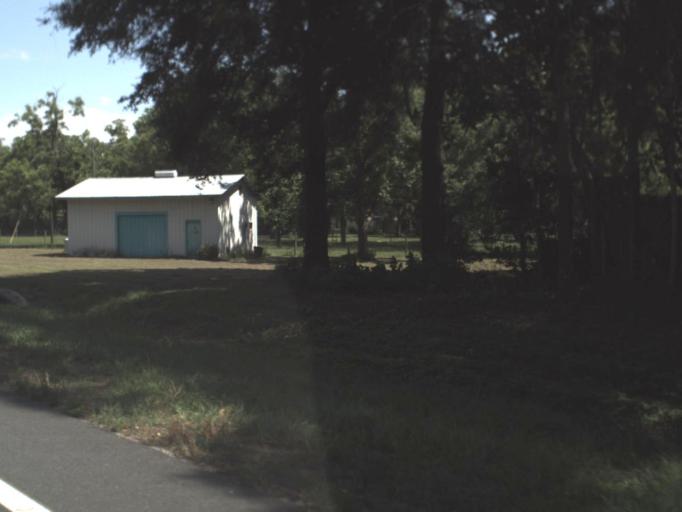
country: US
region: Florida
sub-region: Lafayette County
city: Mayo
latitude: 30.0681
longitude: -83.1989
